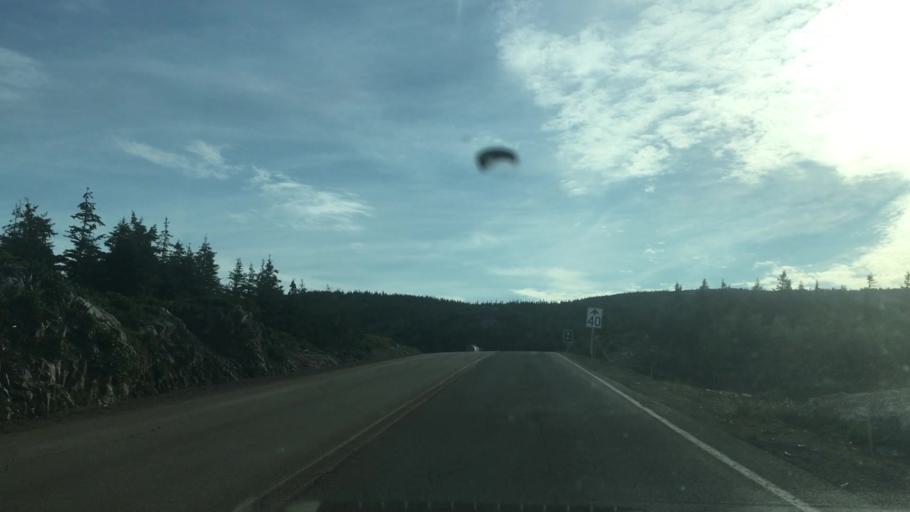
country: CA
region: Nova Scotia
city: Sydney Mines
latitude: 46.8188
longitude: -60.8326
